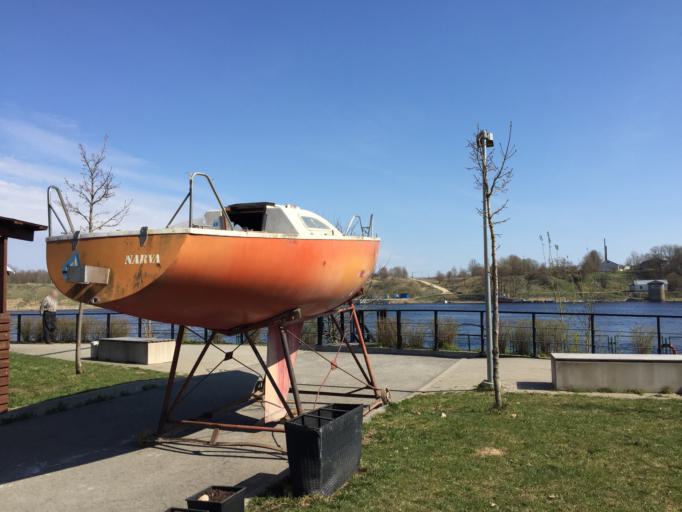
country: RU
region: Leningrad
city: Ivangorod
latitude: 59.3836
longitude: 28.2057
